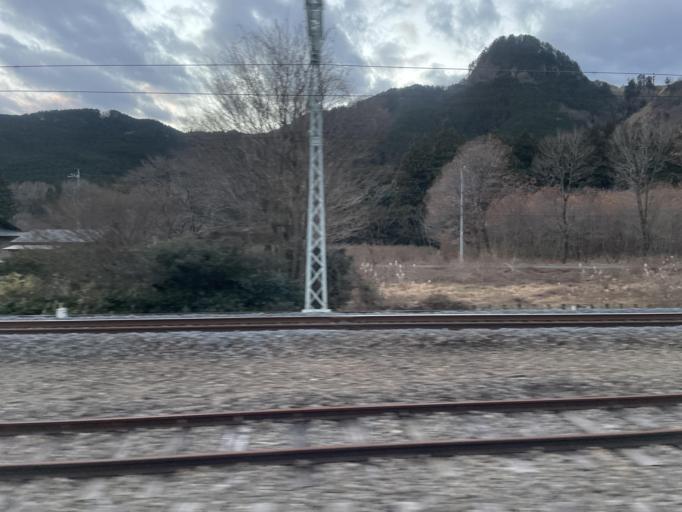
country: JP
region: Tochigi
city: Kanuma
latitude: 36.6184
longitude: 139.7082
